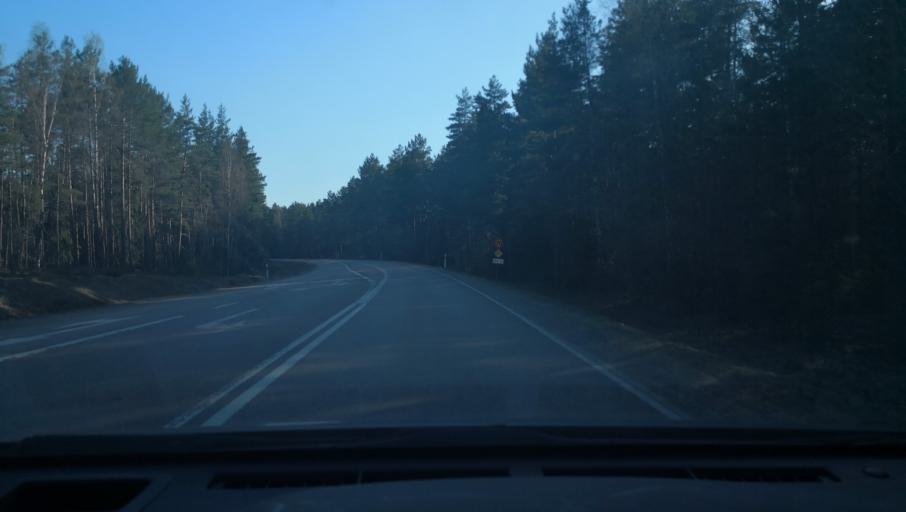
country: SE
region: Uppsala
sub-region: Heby Kommun
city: Heby
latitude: 60.0115
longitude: 16.8399
